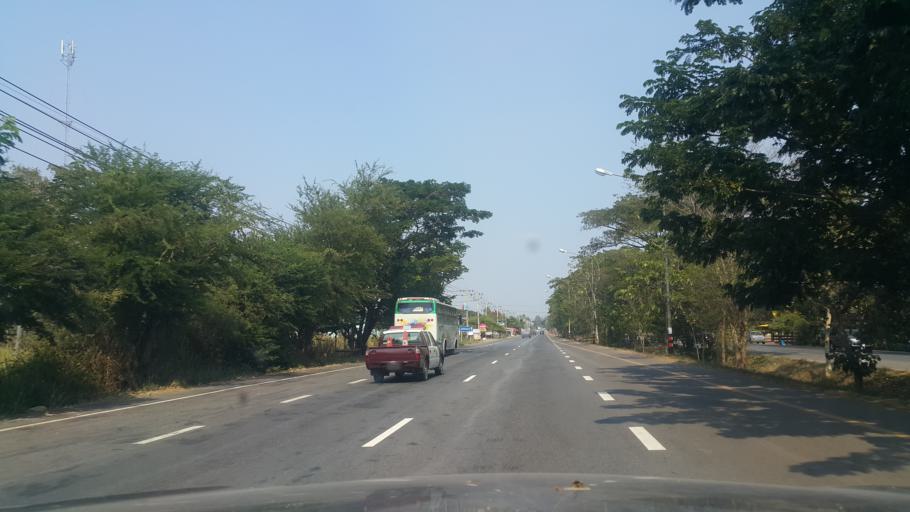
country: TH
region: Nakhon Ratchasima
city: Wang Nam Khiao
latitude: 14.5120
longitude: 101.9565
